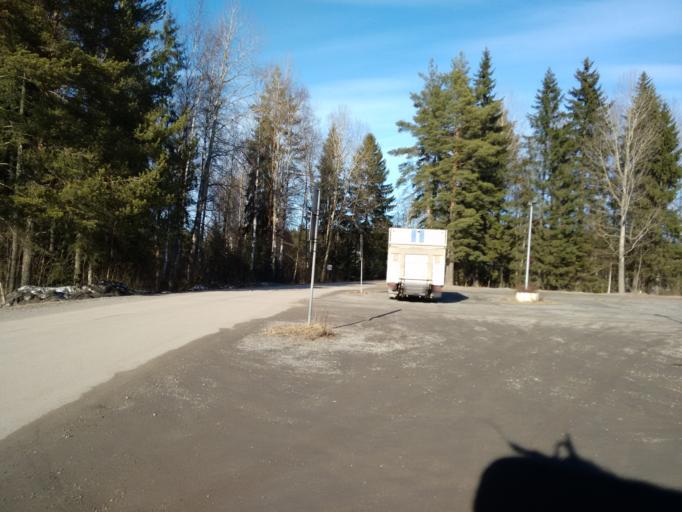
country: FI
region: Pirkanmaa
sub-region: Tampere
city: Tampere
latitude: 61.4615
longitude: 23.7817
